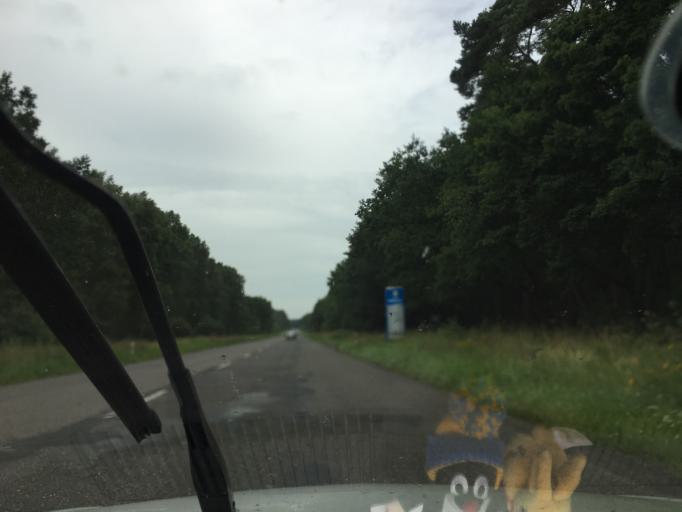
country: PL
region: West Pomeranian Voivodeship
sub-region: Powiat gryficki
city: Pobierowo
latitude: 54.0456
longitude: 14.9065
